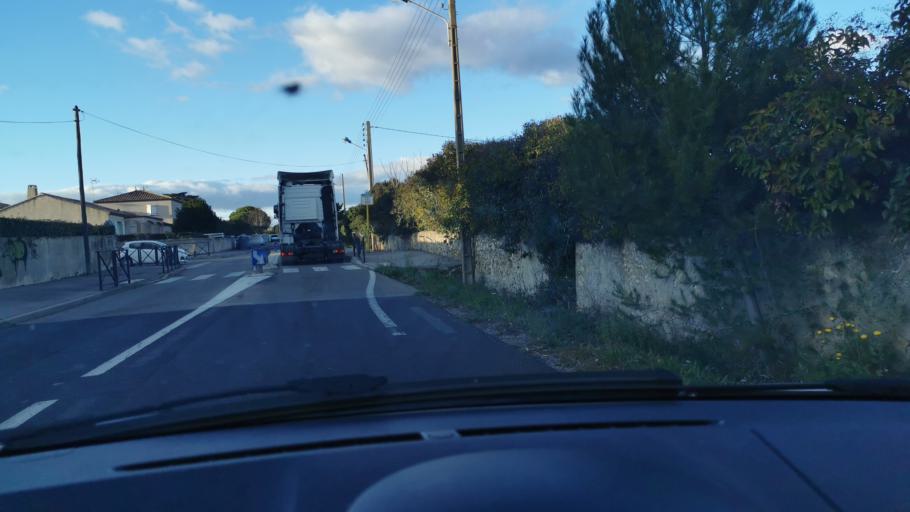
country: FR
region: Languedoc-Roussillon
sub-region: Departement de l'Herault
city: Frontignan
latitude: 43.4316
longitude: 3.7239
